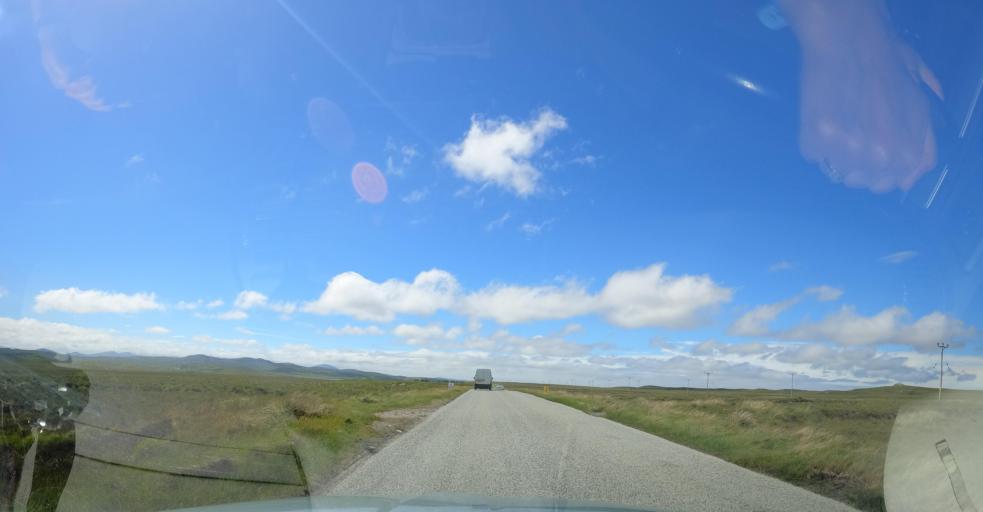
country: GB
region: Scotland
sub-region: Eilean Siar
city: Isle of Lewis
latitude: 58.1861
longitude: -6.6820
